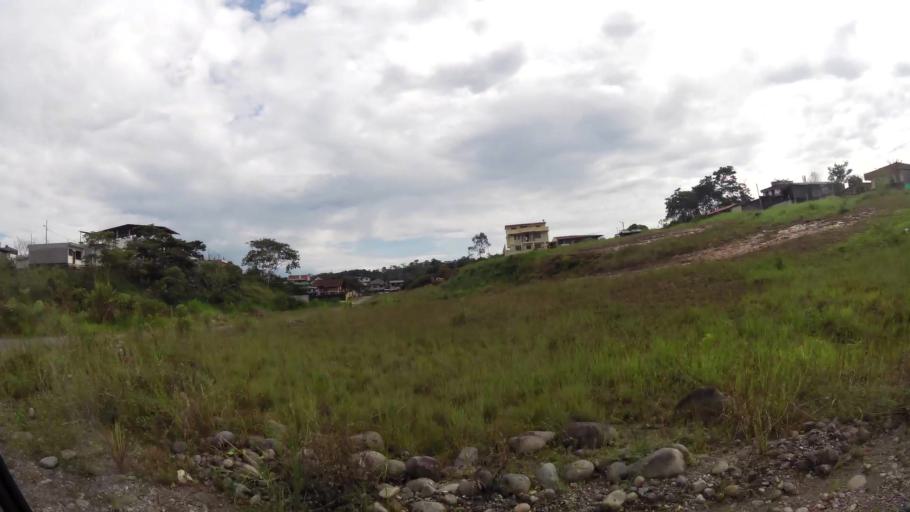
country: EC
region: Pastaza
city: Puyo
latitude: -1.4945
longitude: -77.9918
